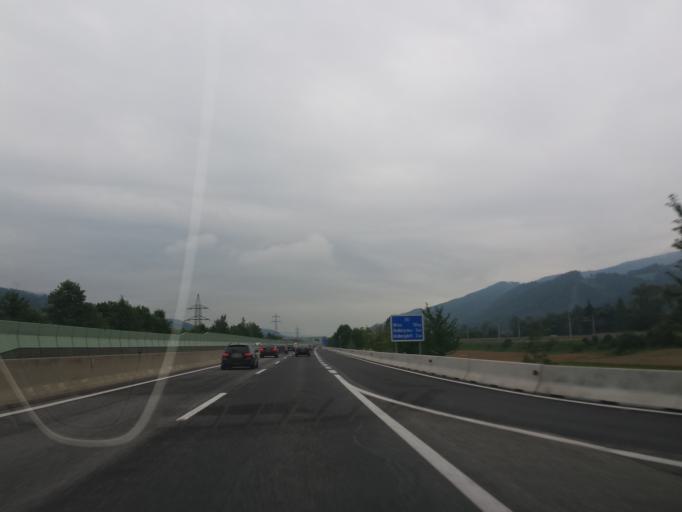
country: AT
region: Styria
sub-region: Politischer Bezirk Bruck-Muerzzuschlag
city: Allerheiligen im Muerztal
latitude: 47.4885
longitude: 15.4119
